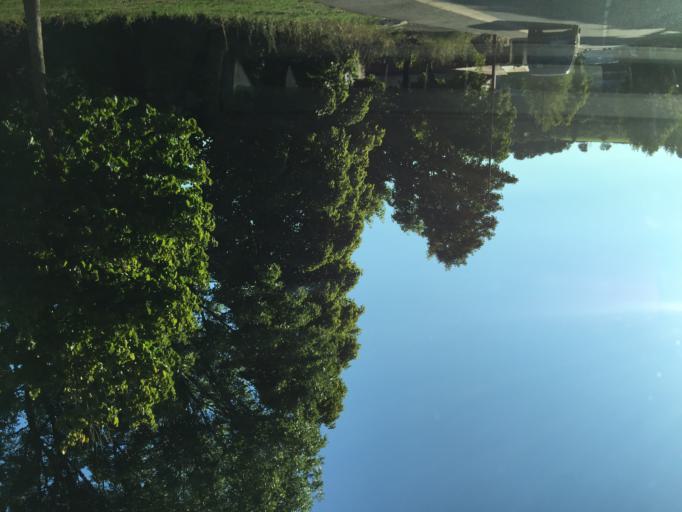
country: FR
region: Midi-Pyrenees
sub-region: Departement de l'Aveyron
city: Salles-Curan
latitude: 44.1830
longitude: 2.7894
